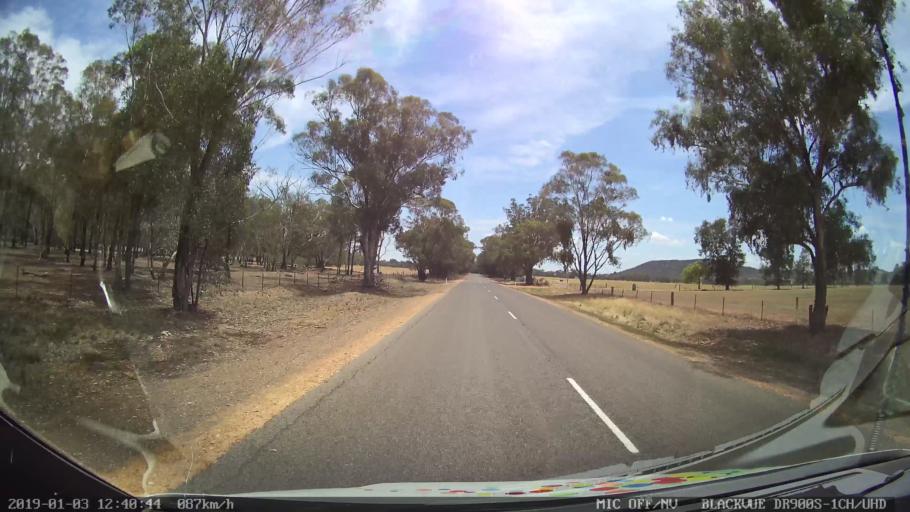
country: AU
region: New South Wales
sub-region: Weddin
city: Grenfell
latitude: -33.8089
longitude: 148.2134
